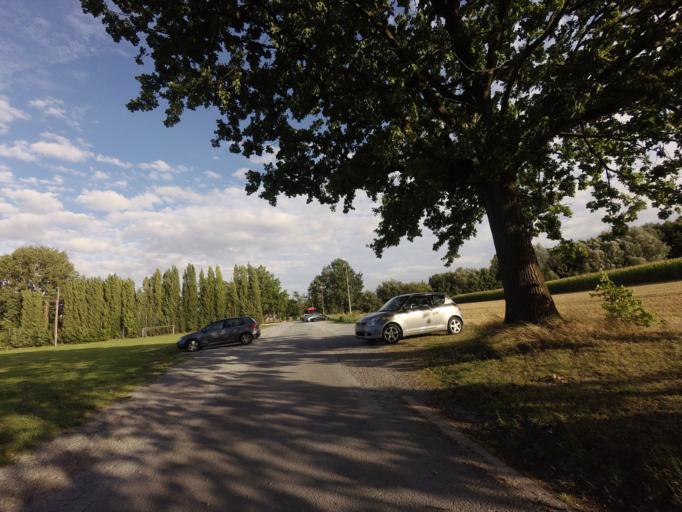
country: BE
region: Flanders
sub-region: Provincie Vlaams-Brabant
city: Grimbergen
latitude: 50.9692
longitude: 4.3886
